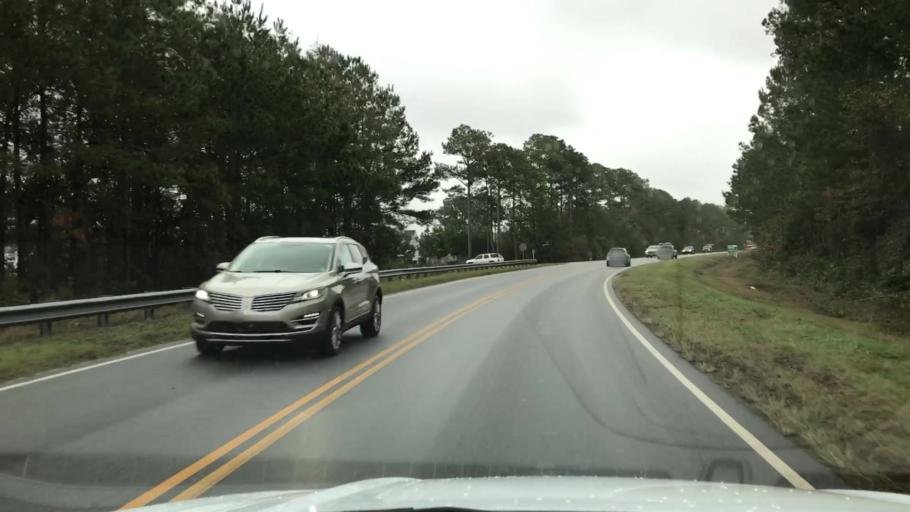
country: US
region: South Carolina
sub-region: Horry County
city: Myrtle Beach
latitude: 33.7551
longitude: -78.8728
